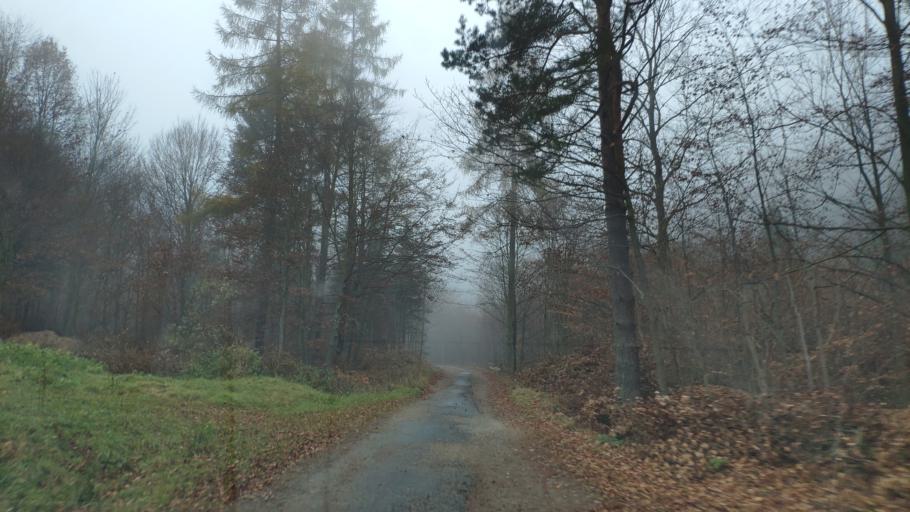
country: SK
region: Presovsky
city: Sabinov
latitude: 49.1545
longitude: 21.2026
